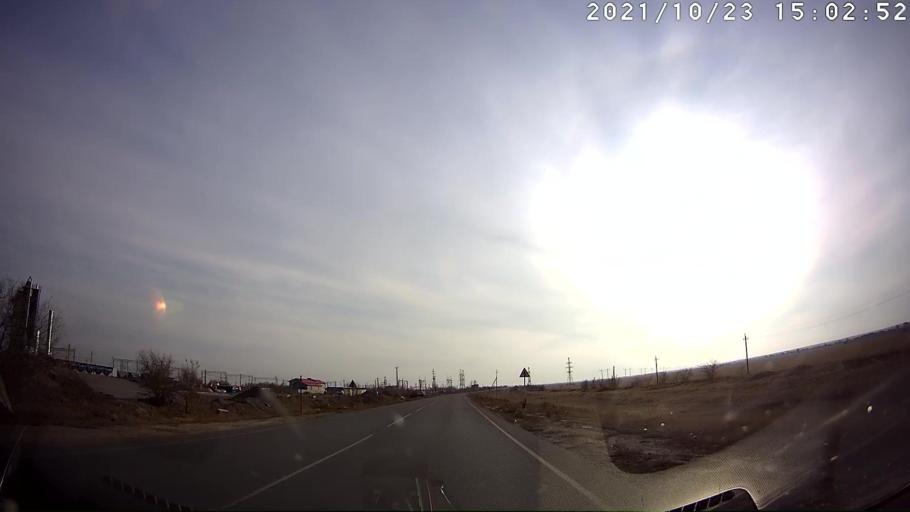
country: RU
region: Volgograd
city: Volgograd
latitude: 48.4211
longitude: 44.3809
